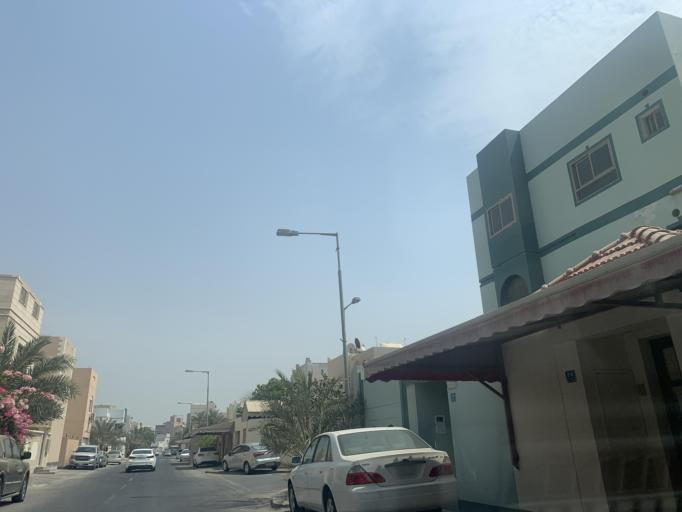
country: BH
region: Manama
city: Jidd Hafs
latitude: 26.2108
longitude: 50.5075
